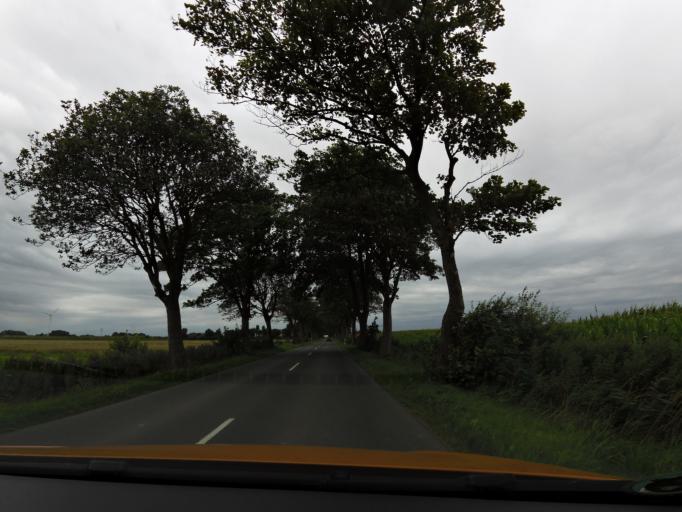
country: DE
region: Lower Saxony
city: Wirdum
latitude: 53.5047
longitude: 7.1849
